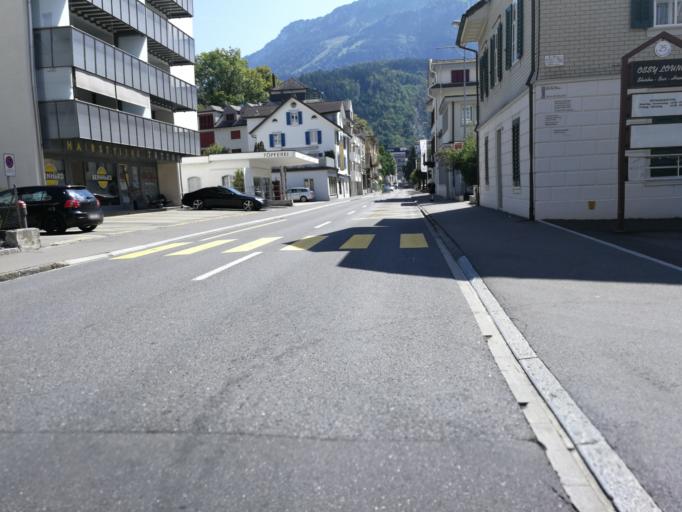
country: CH
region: Schwyz
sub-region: Bezirk Schwyz
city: Ingenbohl
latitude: 46.9958
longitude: 8.6020
